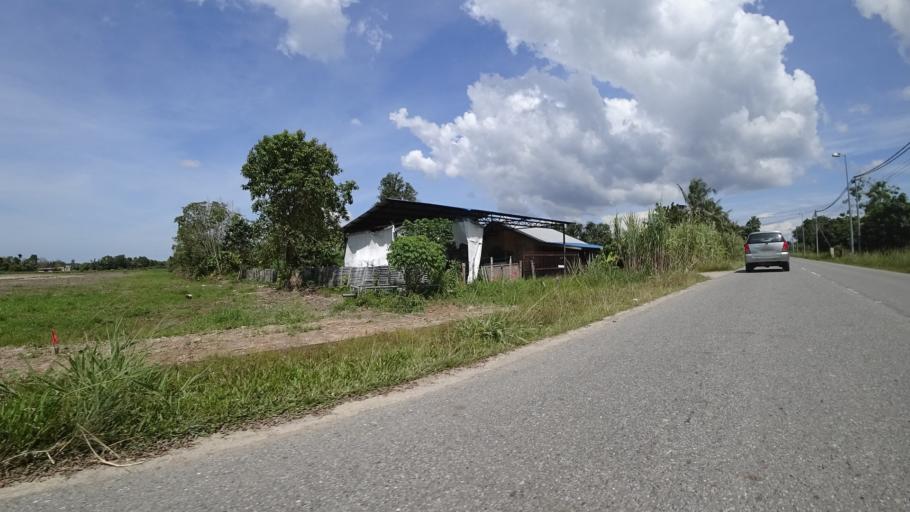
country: BN
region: Brunei and Muara
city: Bandar Seri Begawan
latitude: 4.8435
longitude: 114.8481
